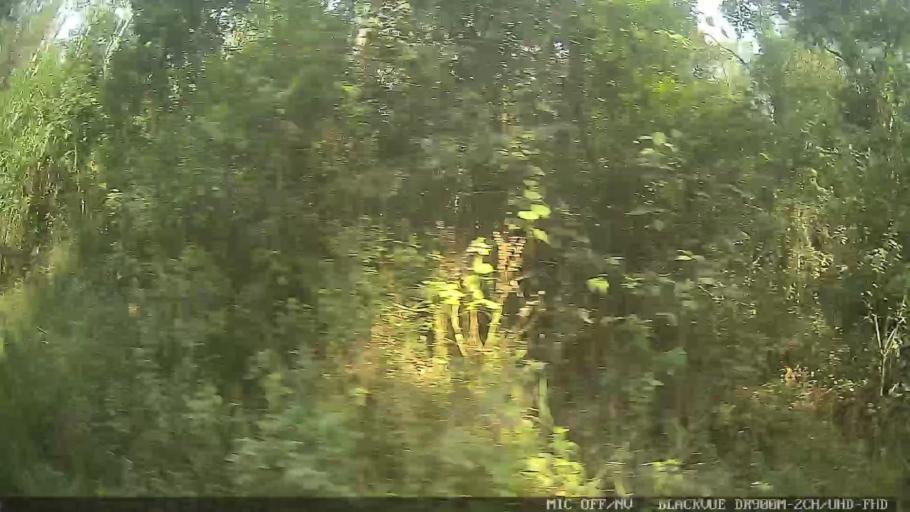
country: BR
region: Sao Paulo
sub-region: Bom Jesus Dos Perdoes
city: Bom Jesus dos Perdoes
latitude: -23.1595
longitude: -46.5146
